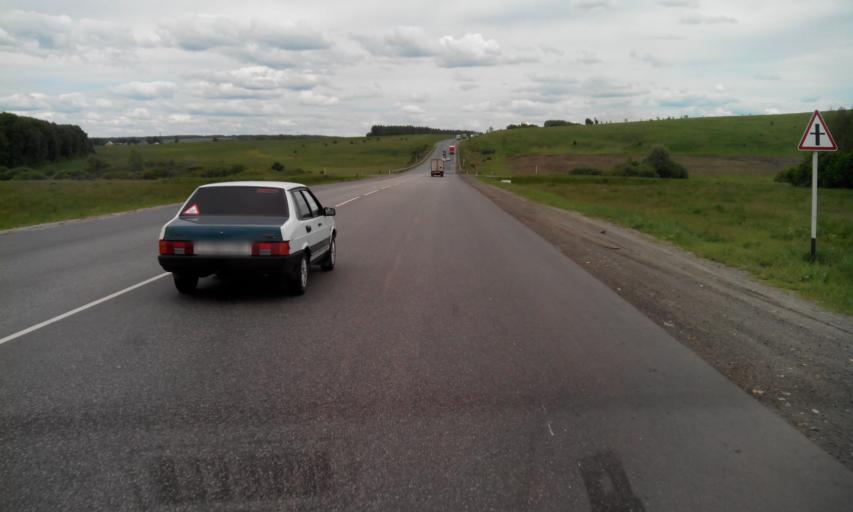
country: RU
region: Penza
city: Chemodanovka
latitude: 53.2376
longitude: 45.3895
